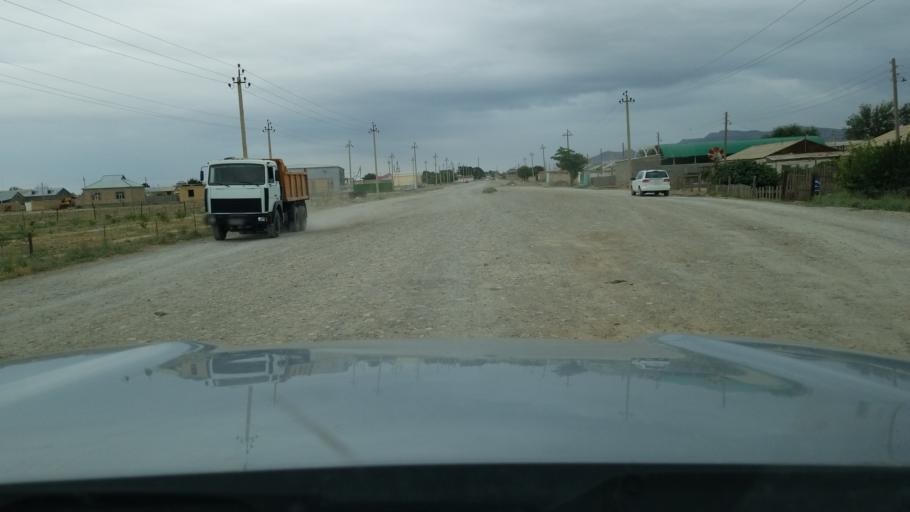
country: TM
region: Balkan
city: Serdar
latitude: 38.9872
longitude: 56.2514
